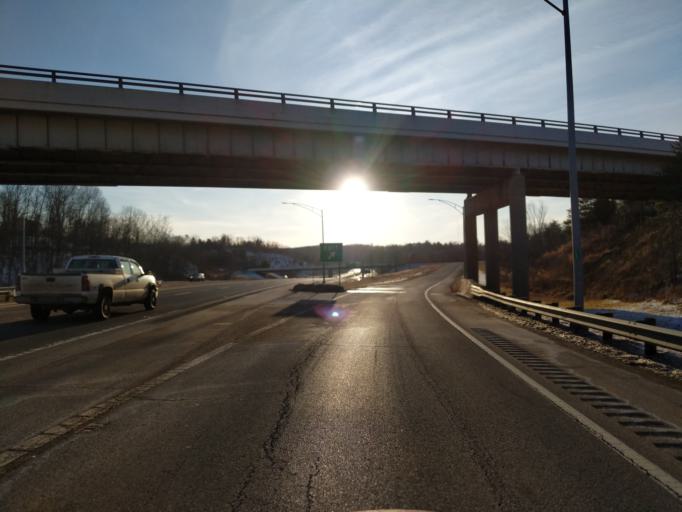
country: US
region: Ohio
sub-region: Athens County
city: Athens
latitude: 39.3158
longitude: -82.0955
